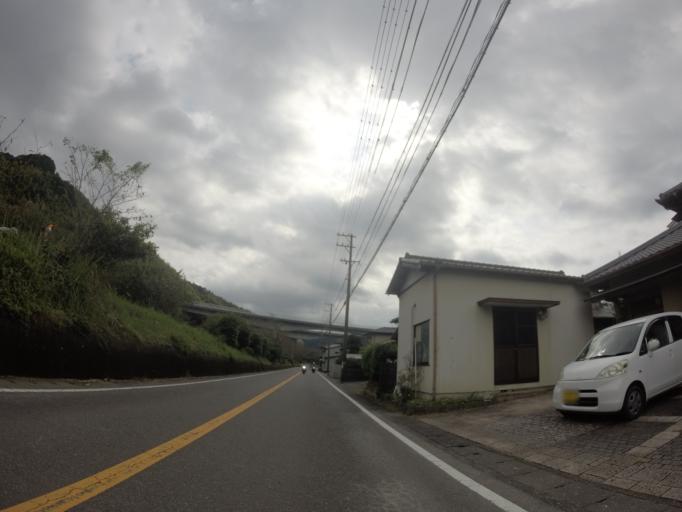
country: JP
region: Shizuoka
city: Fujieda
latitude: 34.8891
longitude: 138.2160
